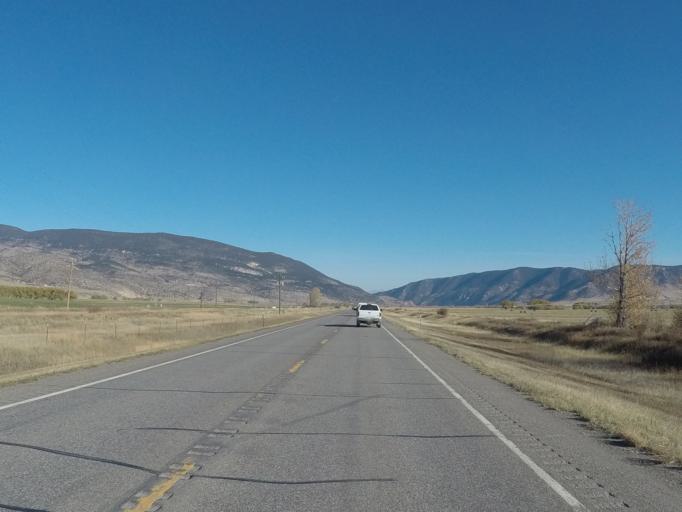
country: US
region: Montana
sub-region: Park County
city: Livingston
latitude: 45.5278
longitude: -110.6064
